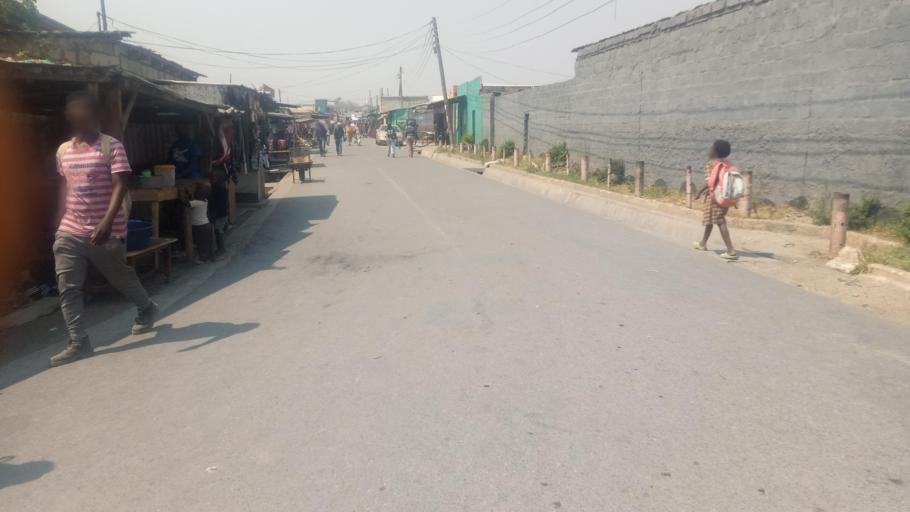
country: ZM
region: Lusaka
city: Lusaka
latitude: -15.4452
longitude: 28.3790
